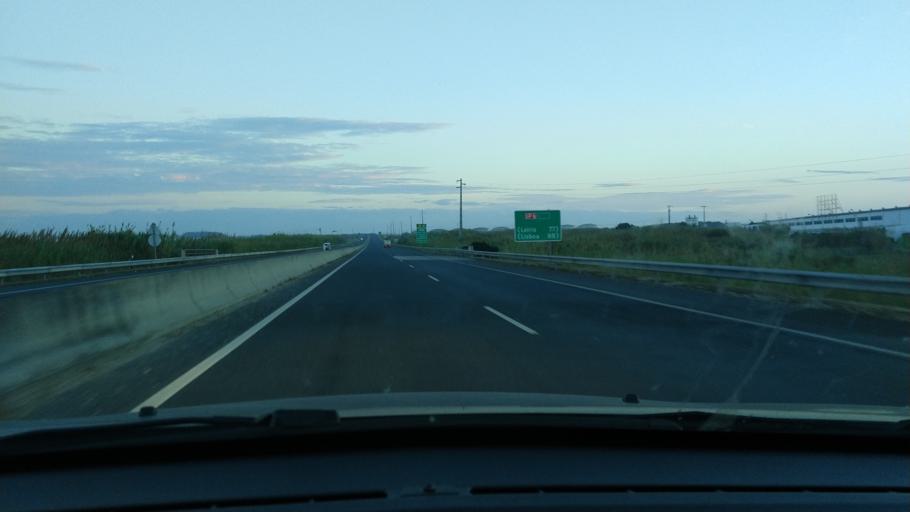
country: PT
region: Leiria
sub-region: Peniche
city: Atouguia da Baleia
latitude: 39.3435
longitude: -9.3400
